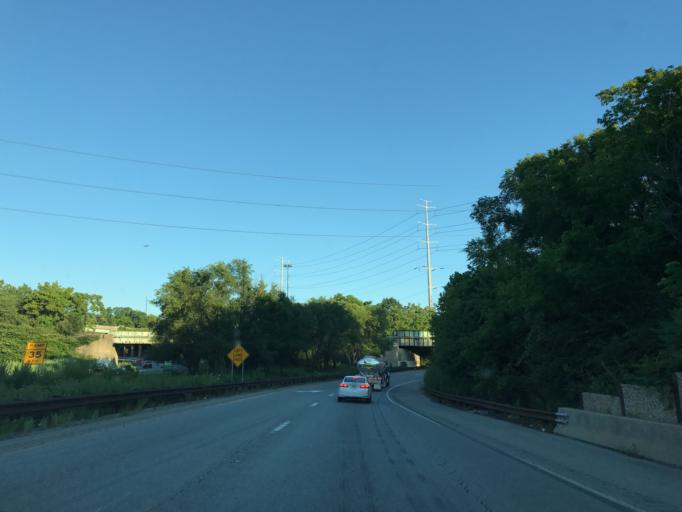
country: US
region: Pennsylvania
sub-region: Delaware County
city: Eddystone
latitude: 39.8691
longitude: -75.3461
